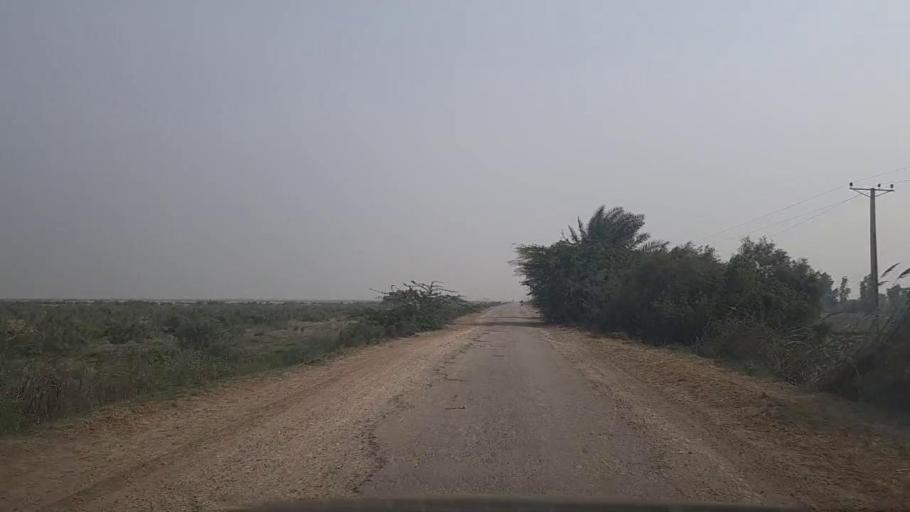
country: PK
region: Sindh
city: Mirpur Sakro
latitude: 24.4700
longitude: 67.6763
